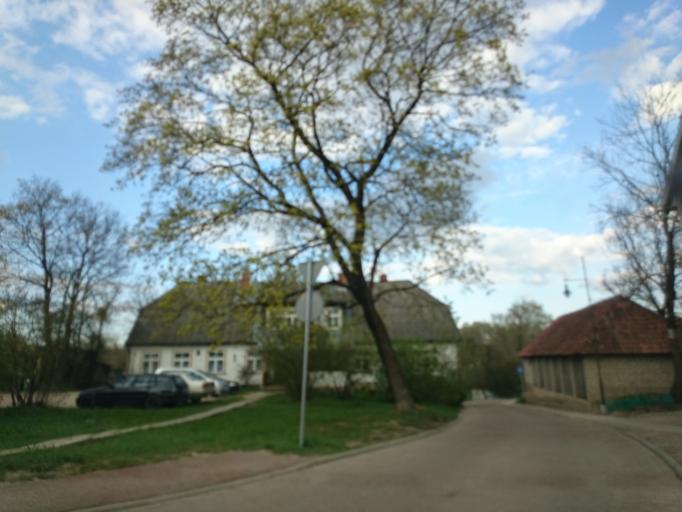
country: LV
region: Kuldigas Rajons
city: Kuldiga
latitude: 56.9715
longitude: 21.9717
